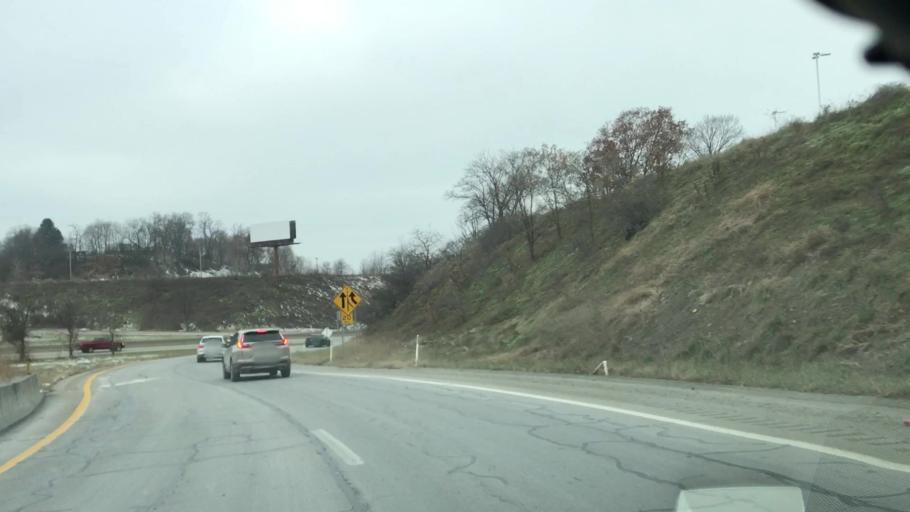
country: US
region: Pennsylvania
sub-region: Allegheny County
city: Oakdale
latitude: 40.4487
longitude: -80.1656
